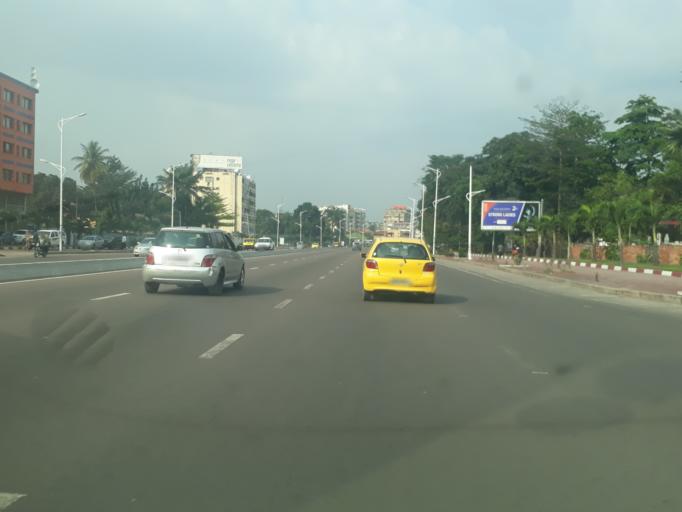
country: CD
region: Kinshasa
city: Kinshasa
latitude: -4.3088
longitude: 15.2920
